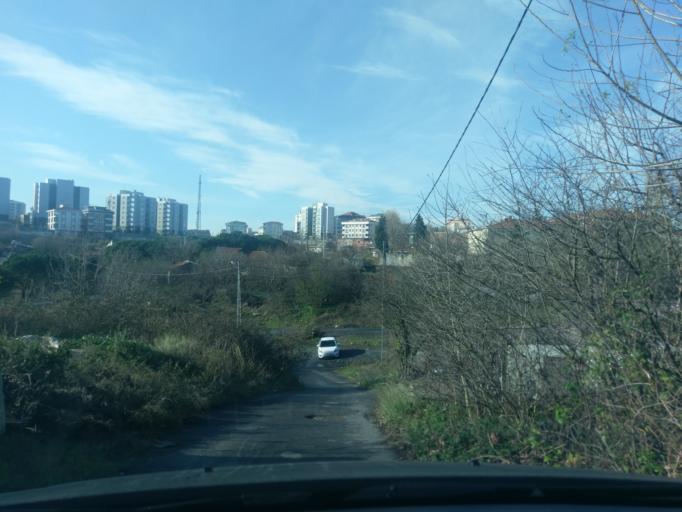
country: TR
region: Istanbul
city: Sultangazi
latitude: 41.1332
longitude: 28.8421
